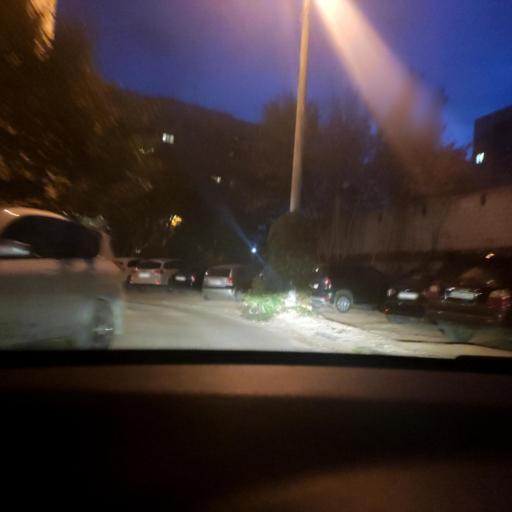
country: RU
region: Samara
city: Samara
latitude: 53.1877
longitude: 50.1413
